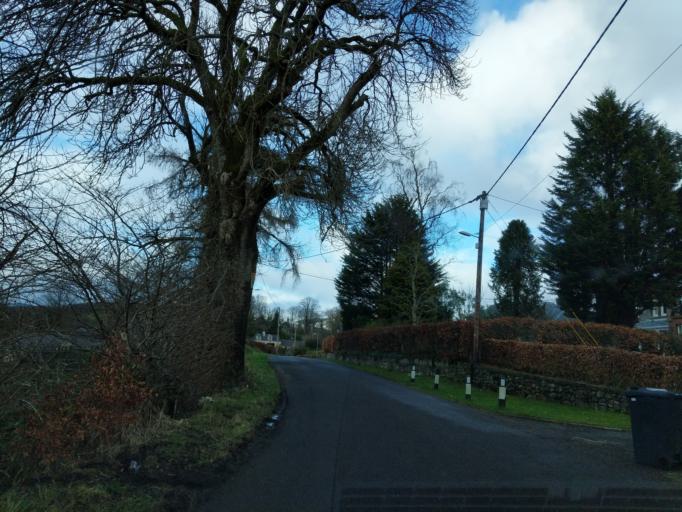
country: GB
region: Scotland
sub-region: Dumfries and Galloway
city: Moffat
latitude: 55.3256
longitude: -3.4307
